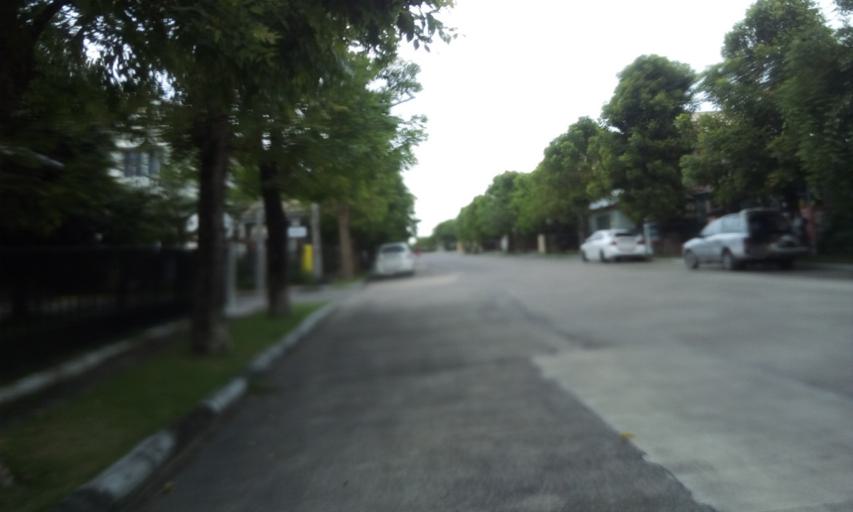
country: TH
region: Pathum Thani
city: Ban Rangsit
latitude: 14.0491
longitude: 100.8288
